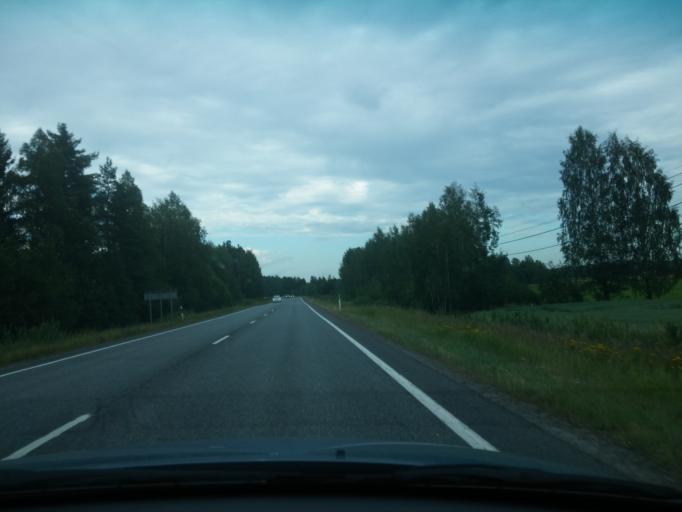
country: FI
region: Haeme
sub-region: Haemeenlinna
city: Tervakoski
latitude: 60.7401
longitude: 24.6193
